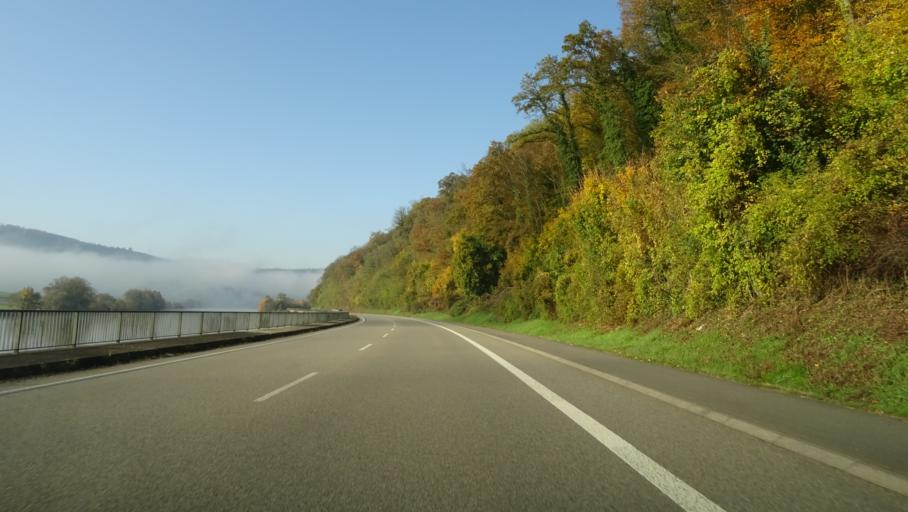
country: DE
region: Baden-Wuerttemberg
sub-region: Karlsruhe Region
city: Binau
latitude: 49.3695
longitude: 9.0776
